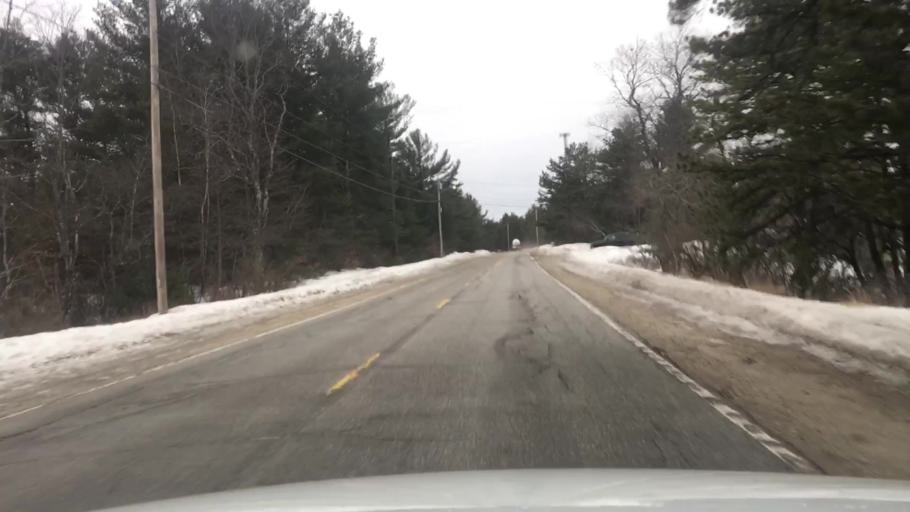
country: US
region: Maine
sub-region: York County
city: Shapleigh
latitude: 43.5708
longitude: -70.8615
